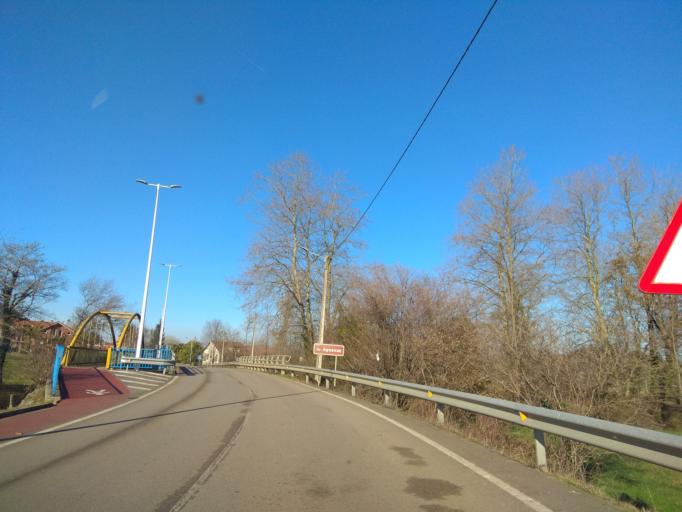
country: ES
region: Cantabria
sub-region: Provincia de Cantabria
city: Entrambasaguas
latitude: 43.3742
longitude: -3.6730
